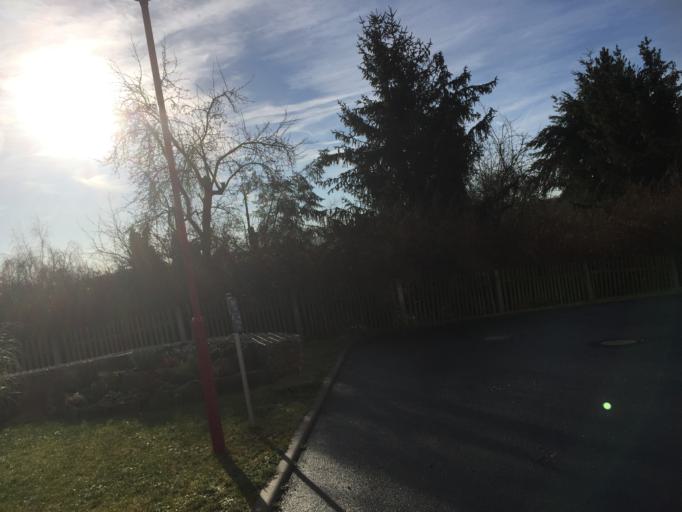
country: DE
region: Thuringia
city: Orlamunde
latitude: 50.7689
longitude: 11.5137
